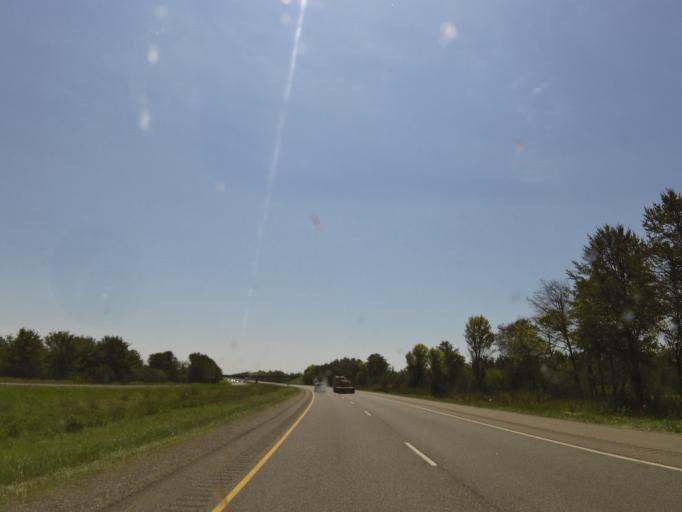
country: US
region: Wisconsin
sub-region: Jackson County
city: Black River Falls
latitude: 44.2808
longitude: -90.8080
